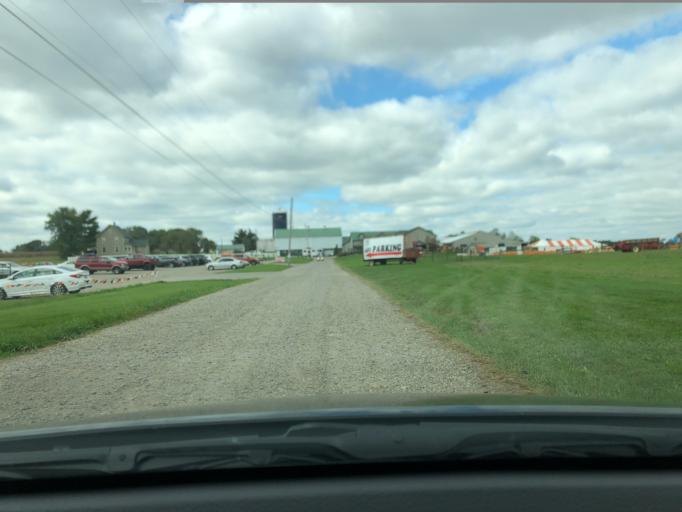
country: US
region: Ohio
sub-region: Stark County
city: Canal Fulton
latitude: 40.8267
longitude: -81.6042
